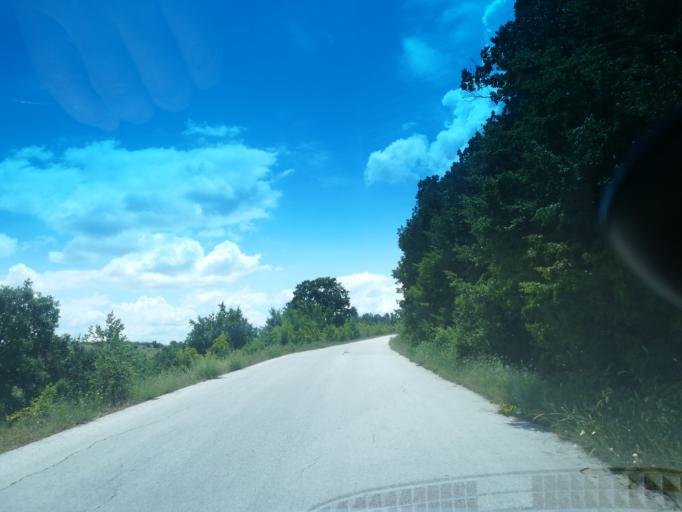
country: BG
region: Khaskovo
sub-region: Obshtina Mineralni Bani
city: Mineralni Bani
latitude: 41.9630
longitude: 25.2612
